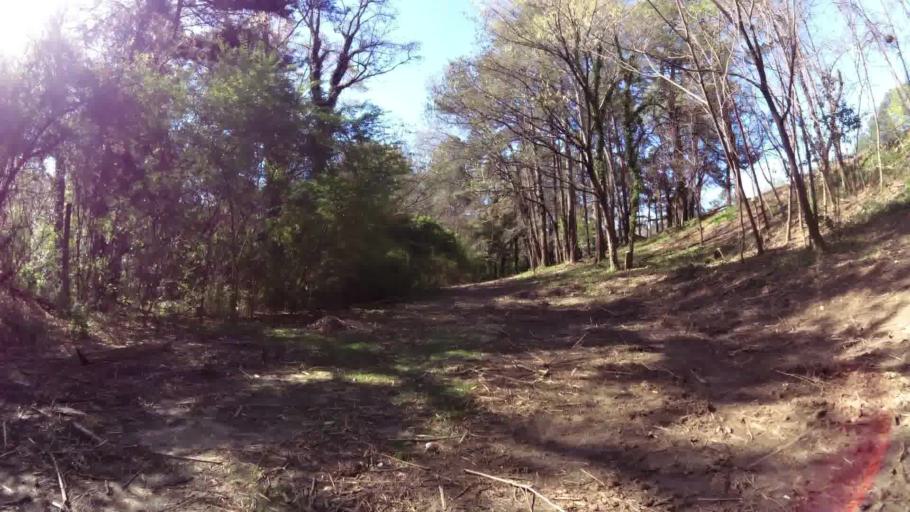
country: US
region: Georgia
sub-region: DeKalb County
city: Scottdale
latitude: 33.8233
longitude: -84.2736
